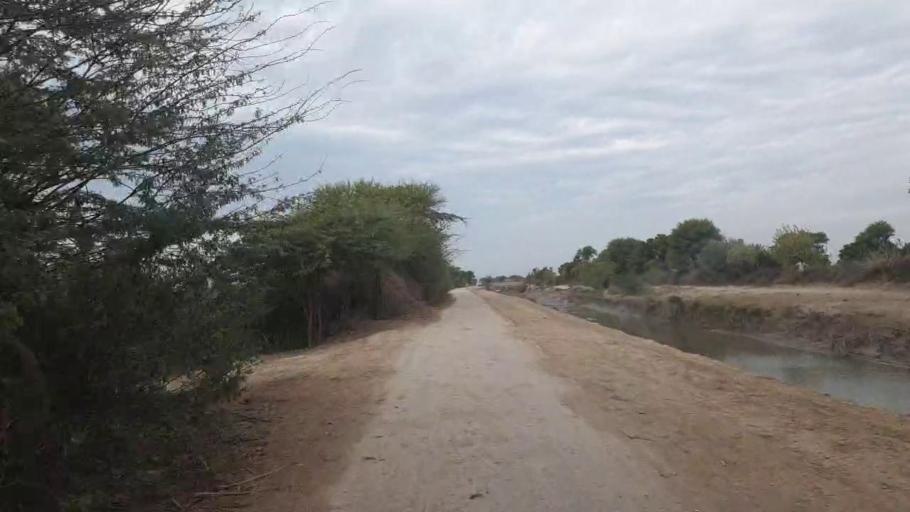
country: PK
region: Sindh
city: Jhol
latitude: 25.9867
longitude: 68.8991
